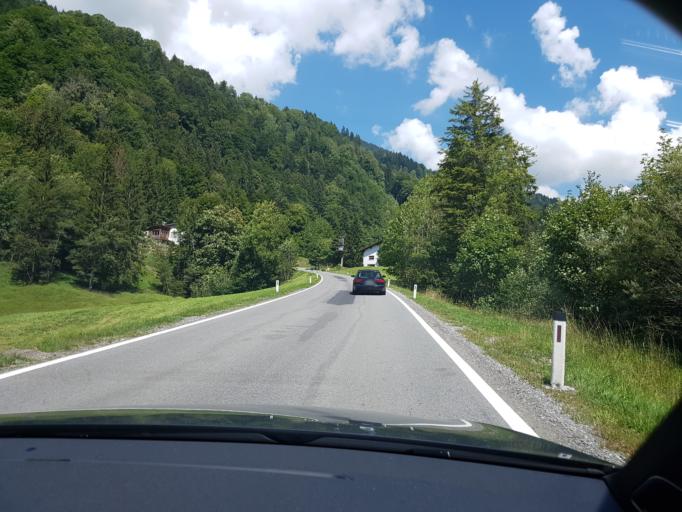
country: AT
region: Vorarlberg
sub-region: Politischer Bezirk Bregenz
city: Damuels
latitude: 47.2315
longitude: 9.8864
